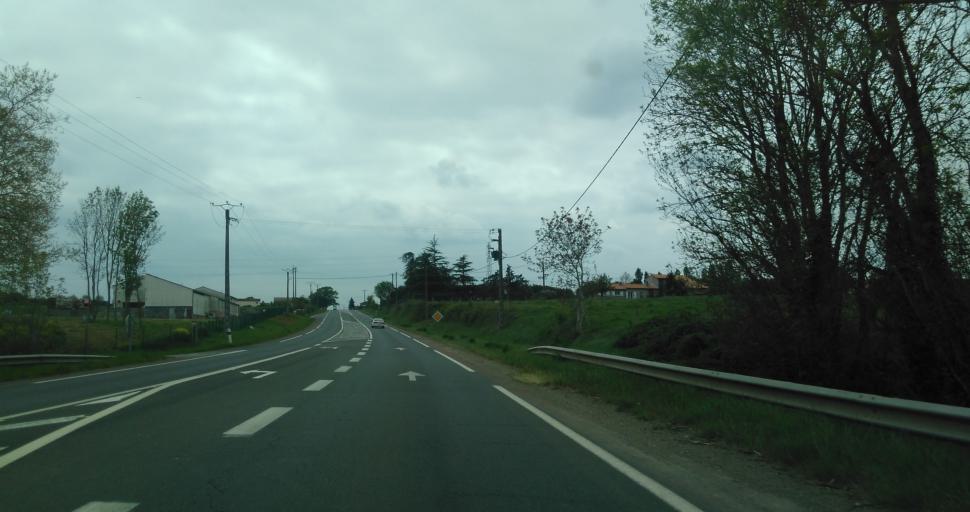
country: FR
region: Poitou-Charentes
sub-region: Departement des Deux-Sevres
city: Niort
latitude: 46.3553
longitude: -0.4384
